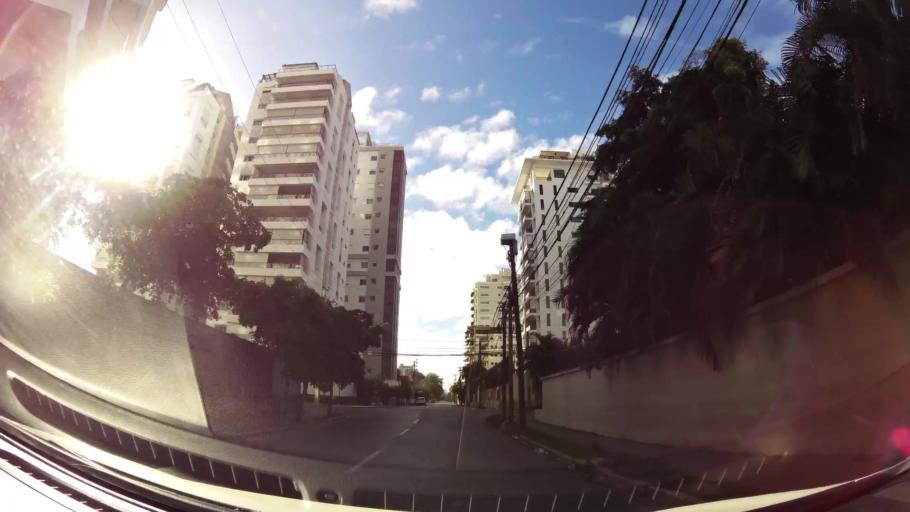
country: DO
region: Nacional
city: La Julia
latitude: 18.4760
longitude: -69.9410
